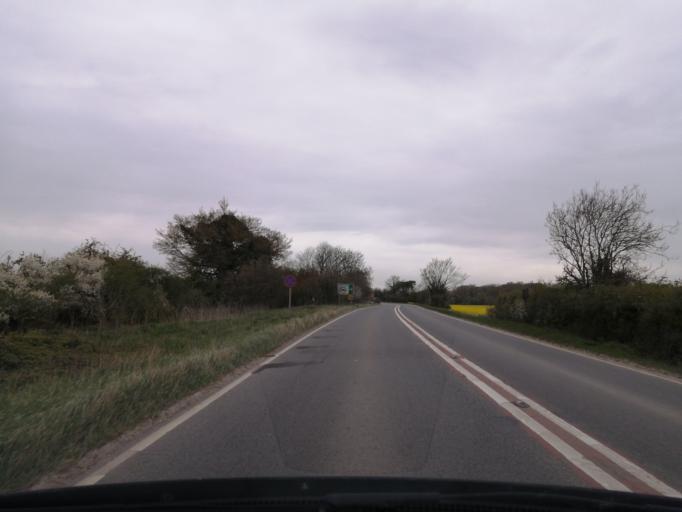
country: GB
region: England
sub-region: Peterborough
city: Thornhaugh
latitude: 52.5878
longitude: -0.4425
